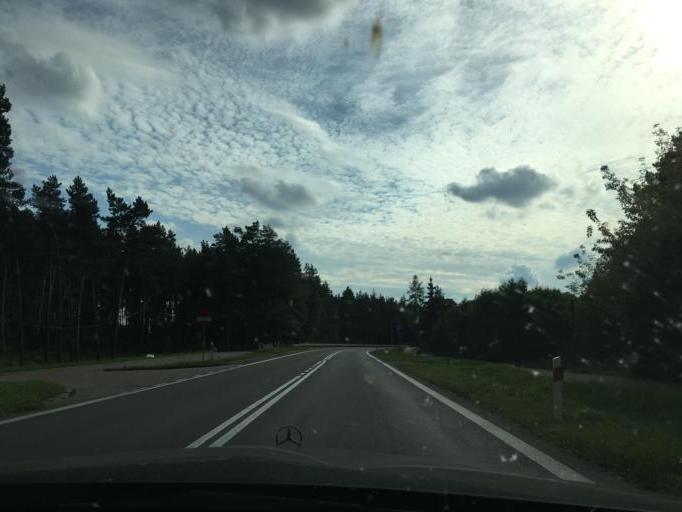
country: PL
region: Podlasie
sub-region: Powiat grajewski
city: Rajgrod
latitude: 53.7093
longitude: 22.6708
